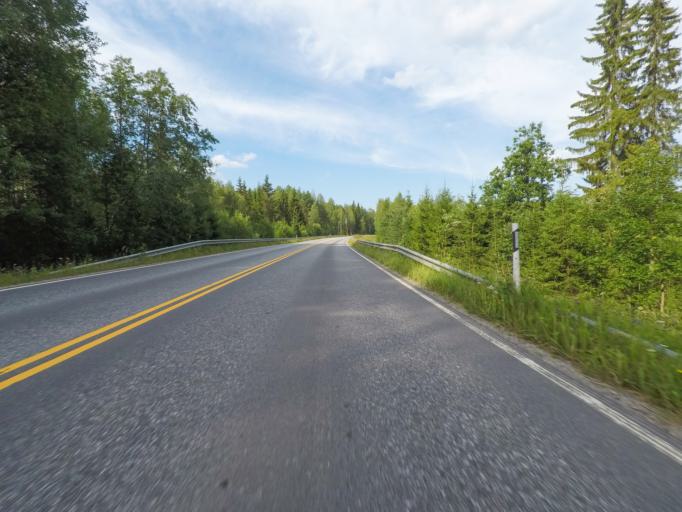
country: FI
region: Southern Savonia
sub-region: Savonlinna
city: Sulkava
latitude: 61.8973
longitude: 28.5785
